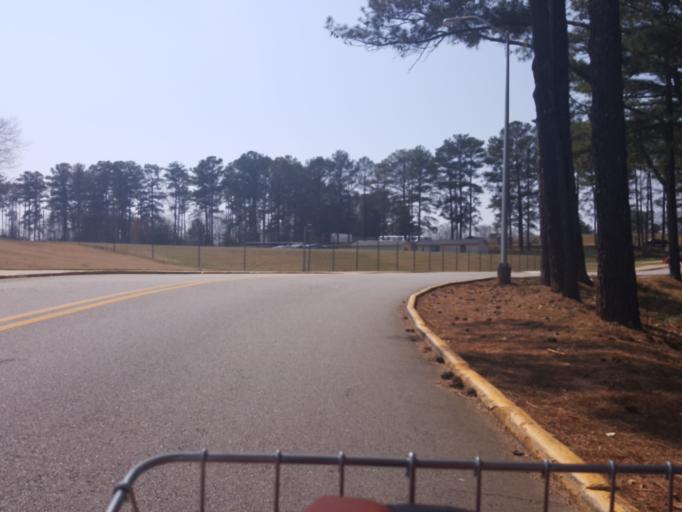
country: US
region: Georgia
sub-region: Carroll County
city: Carrollton
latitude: 33.5730
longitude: -85.1066
